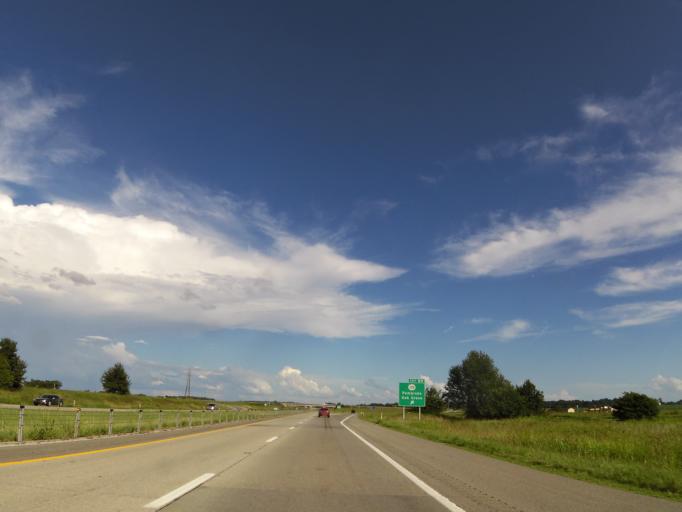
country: US
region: Kentucky
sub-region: Christian County
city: Oak Grove
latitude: 36.6847
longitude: -87.4111
